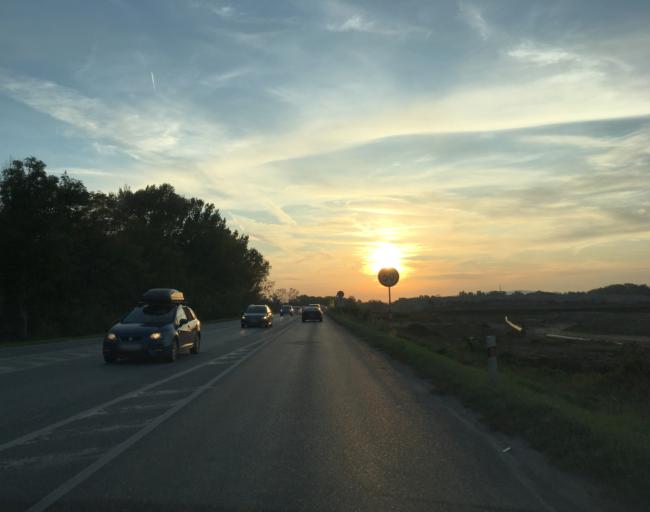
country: SK
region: Bratislavsky
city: Svaty Jur
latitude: 48.1941
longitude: 17.2407
